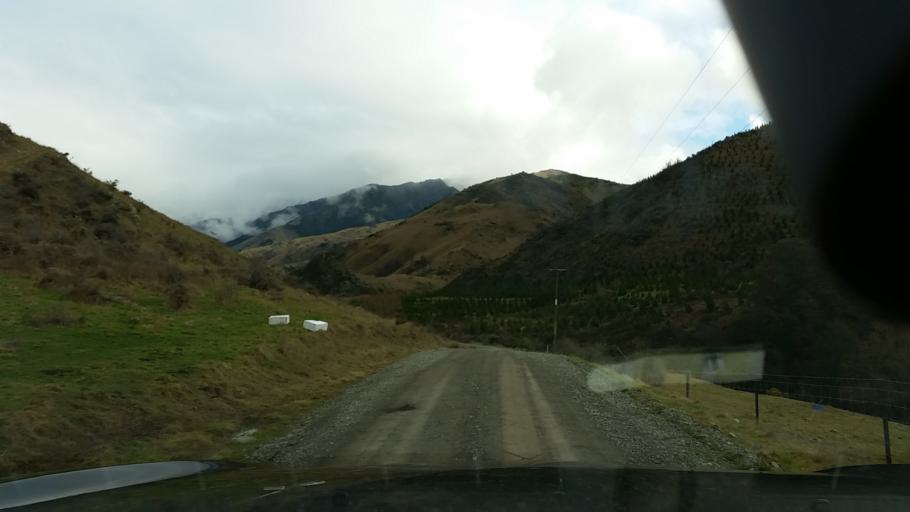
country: NZ
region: Tasman
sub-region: Tasman District
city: Richmond
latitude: -41.7296
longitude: 173.4449
